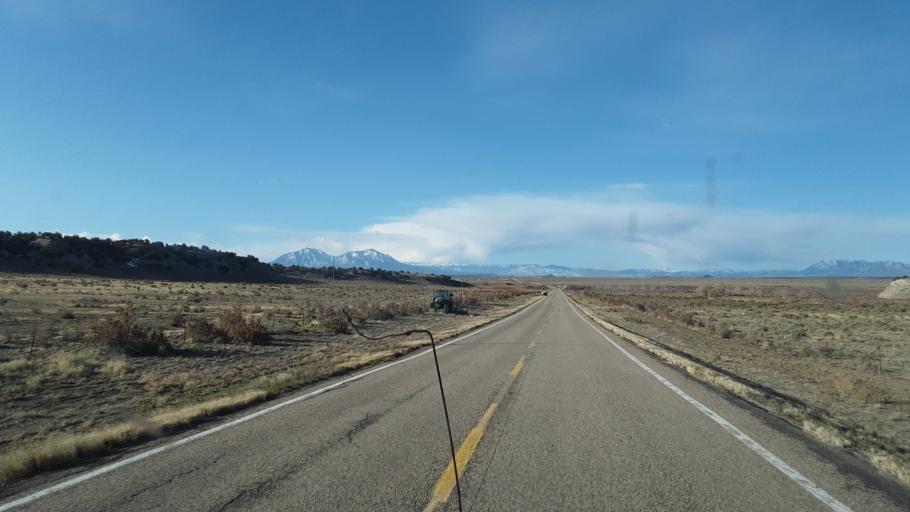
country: US
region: Colorado
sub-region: Huerfano County
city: Walsenburg
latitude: 37.6871
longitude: -104.6411
